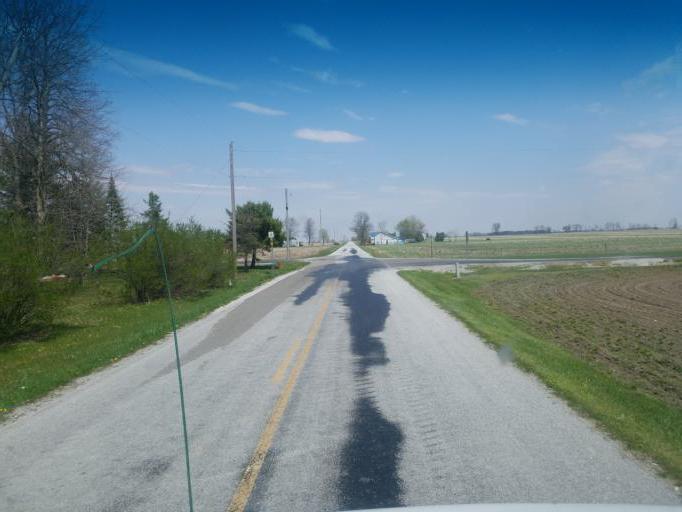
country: US
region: Ohio
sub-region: Hardin County
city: Forest
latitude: 40.7448
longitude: -83.5377
